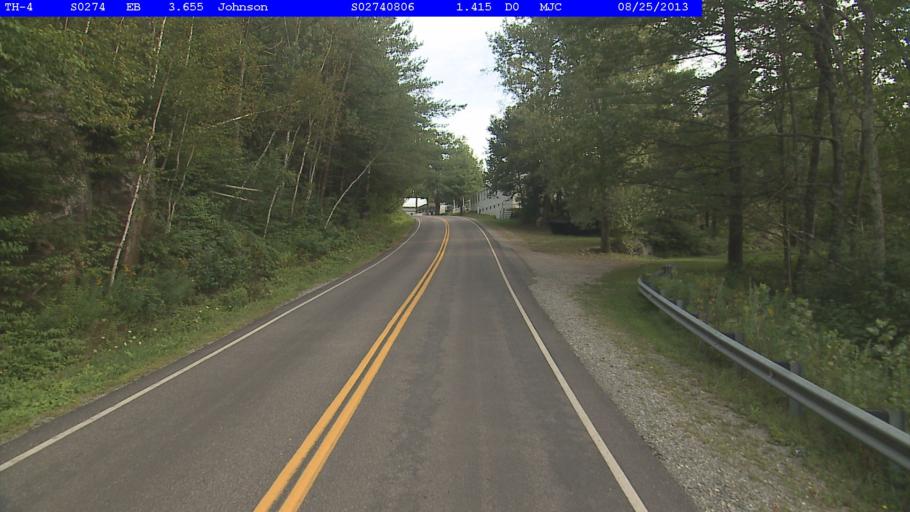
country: US
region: Vermont
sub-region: Lamoille County
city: Johnson
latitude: 44.6500
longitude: -72.7255
